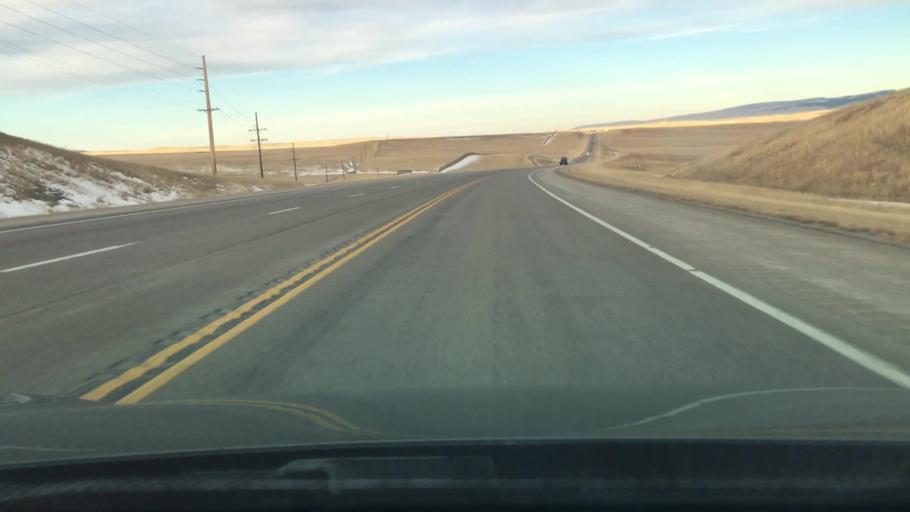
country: US
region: Montana
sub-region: Wheatland County
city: Harlowton
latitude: 46.6356
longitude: -109.7624
